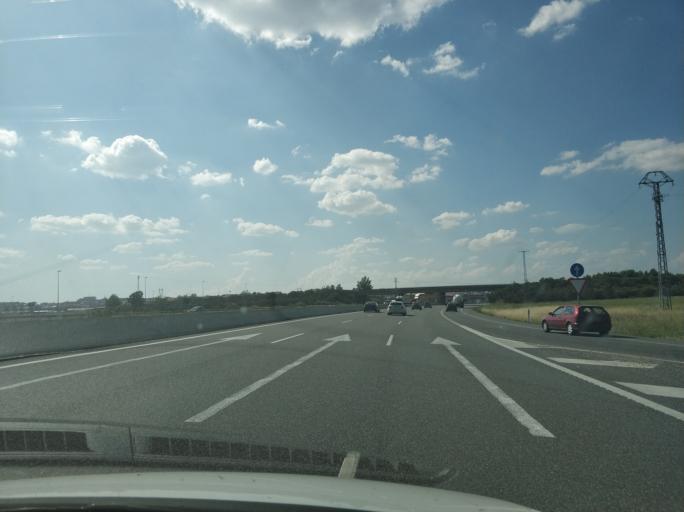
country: ES
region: Castille and Leon
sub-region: Provincia de Zamora
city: Benavente
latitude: 41.9985
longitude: -5.6547
